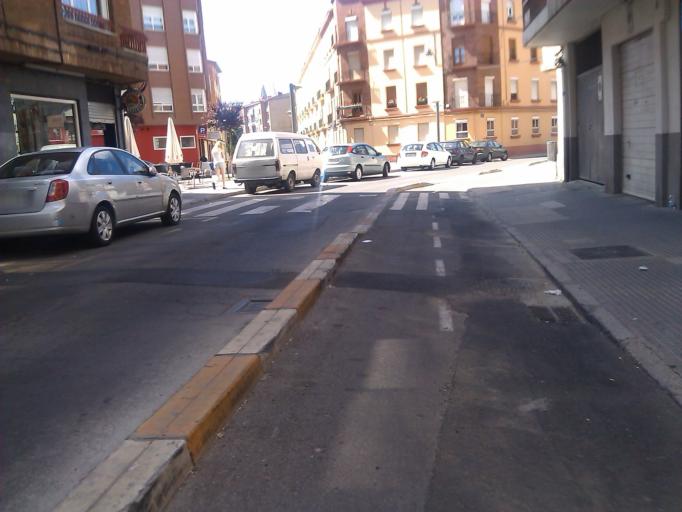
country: ES
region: Castille and Leon
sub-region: Provincia de Leon
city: Leon
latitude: 42.6048
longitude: -5.5673
